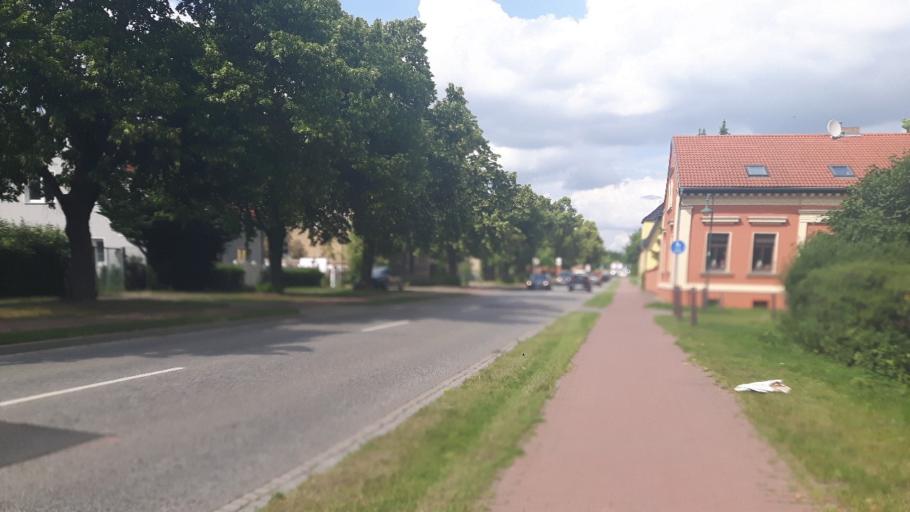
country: DE
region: Berlin
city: Buch
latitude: 52.6280
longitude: 13.5449
